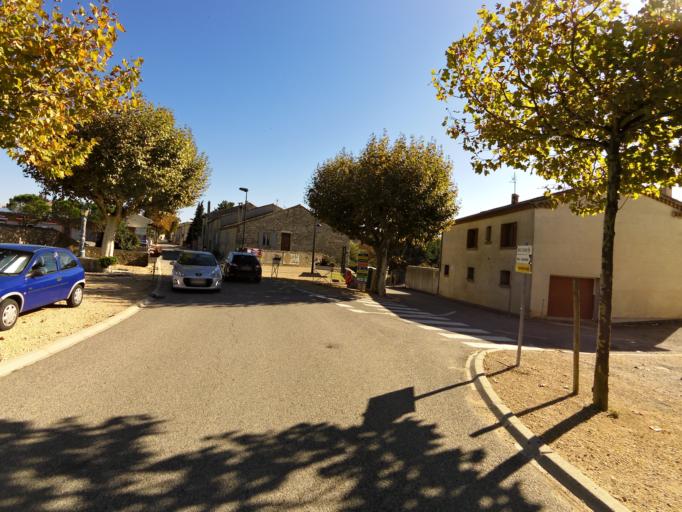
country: FR
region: Languedoc-Roussillon
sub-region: Departement du Gard
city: Saint-Julien-de-Peyrolas
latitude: 44.3935
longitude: 4.4986
